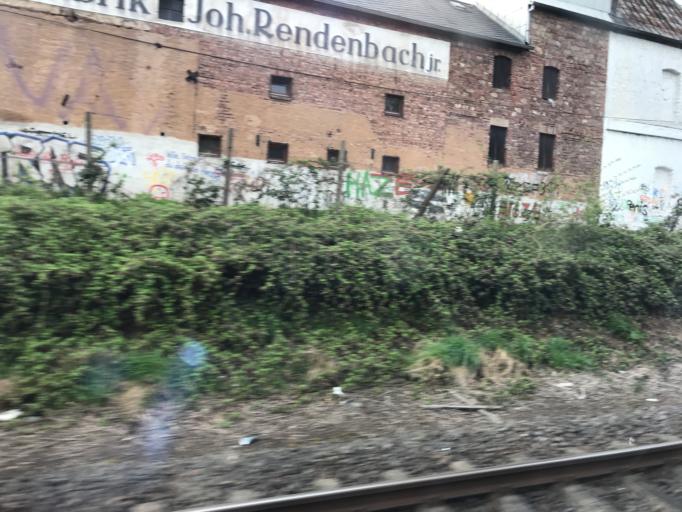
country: DE
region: Rheinland-Pfalz
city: Trier
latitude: 49.7469
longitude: 6.6399
